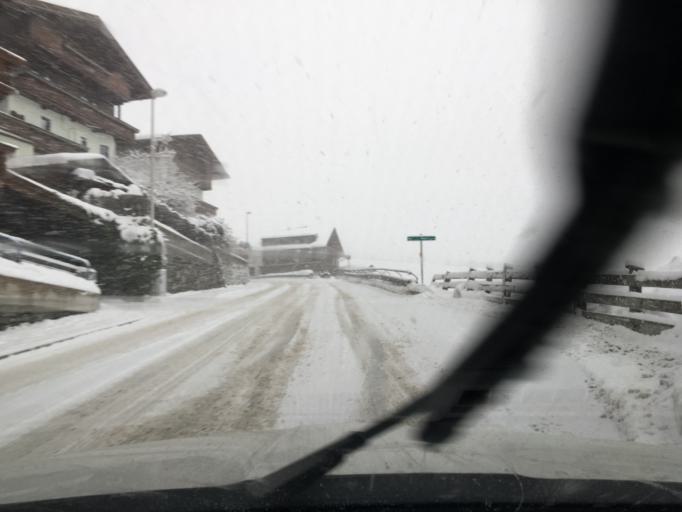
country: AT
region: Tyrol
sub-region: Politischer Bezirk Schwaz
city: Mayrhofen
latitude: 47.1521
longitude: 11.8186
